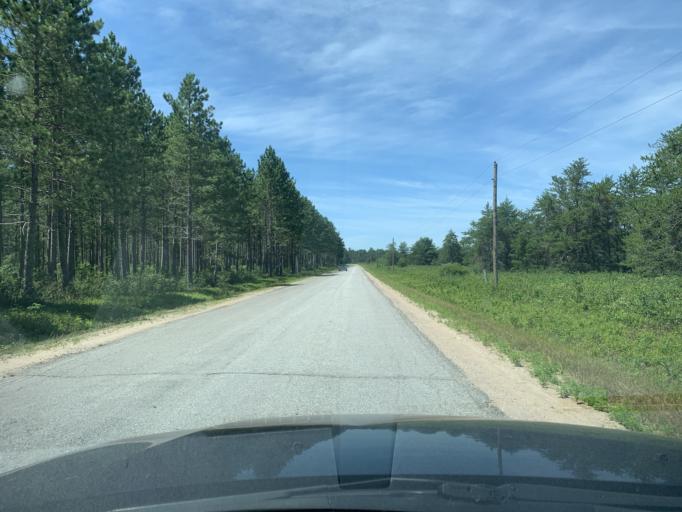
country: CA
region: Ontario
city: Petawawa
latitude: 45.6597
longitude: -77.5837
